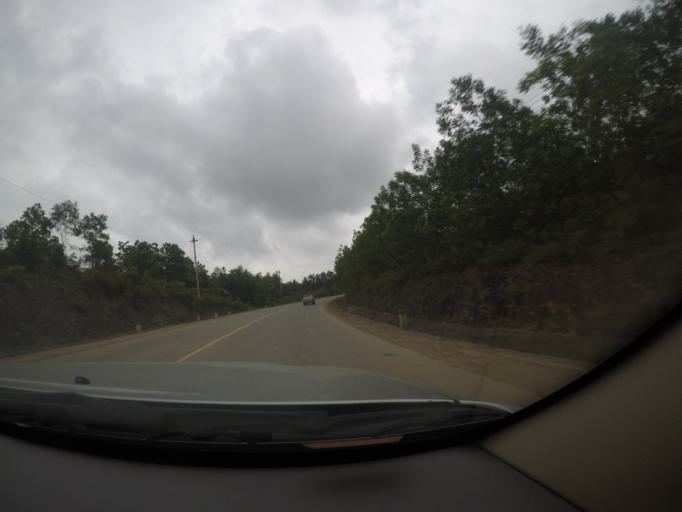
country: VN
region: Quang Tri
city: Cam Lo
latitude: 16.7990
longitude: 107.0444
